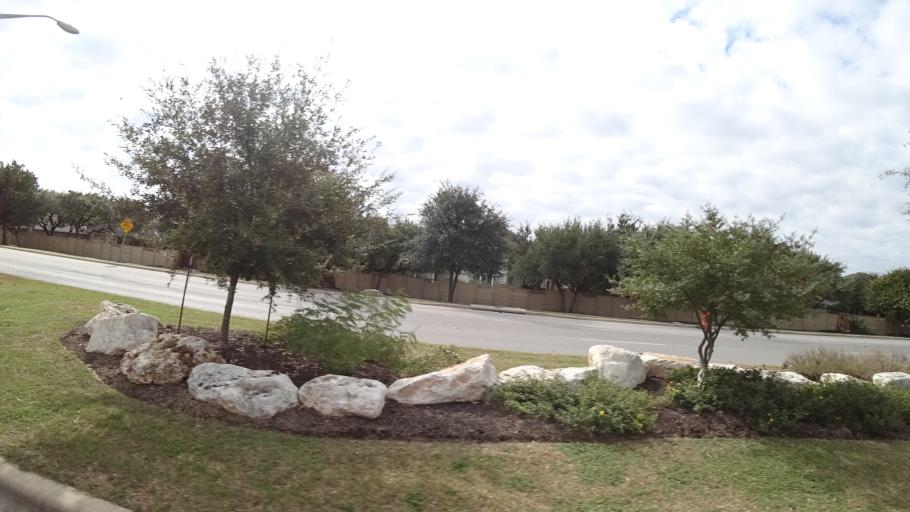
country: US
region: Texas
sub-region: Williamson County
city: Cedar Park
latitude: 30.4872
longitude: -97.8558
